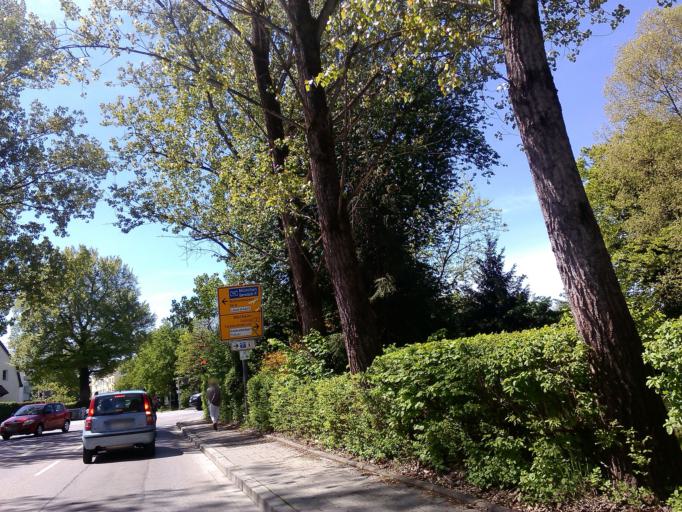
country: DE
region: Bavaria
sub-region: Upper Bavaria
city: Starnberg
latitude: 48.0025
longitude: 11.3492
